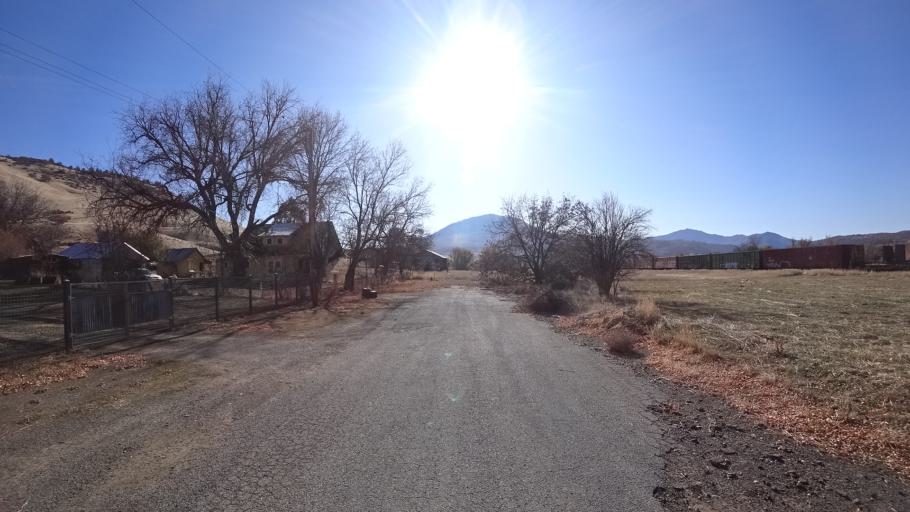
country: US
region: California
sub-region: Siskiyou County
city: Montague
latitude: 41.9083
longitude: -122.5523
